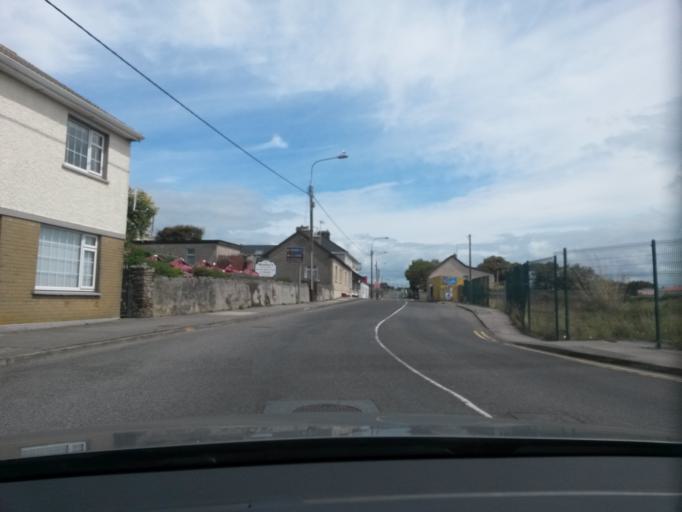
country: IE
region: Ulster
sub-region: County Donegal
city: Bundoran
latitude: 54.4827
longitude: -8.2676
